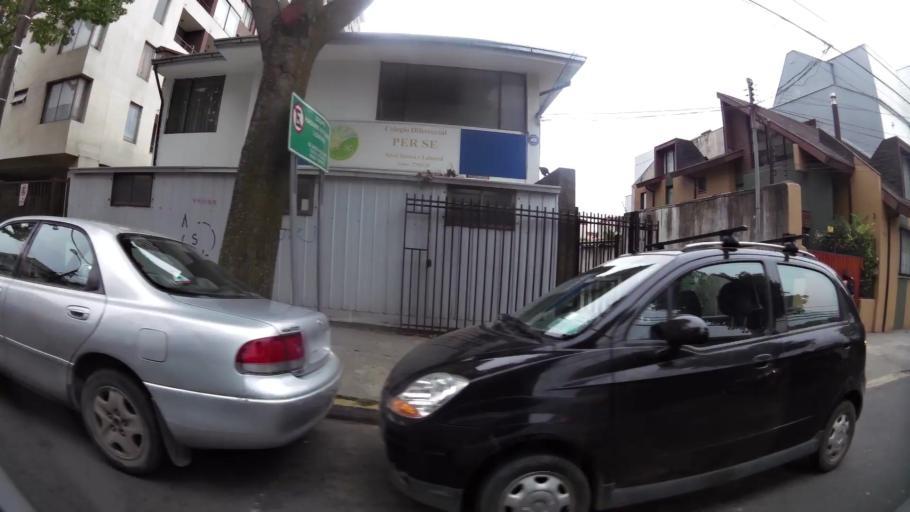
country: CL
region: Biobio
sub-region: Provincia de Concepcion
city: Concepcion
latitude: -36.8203
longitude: -73.0388
